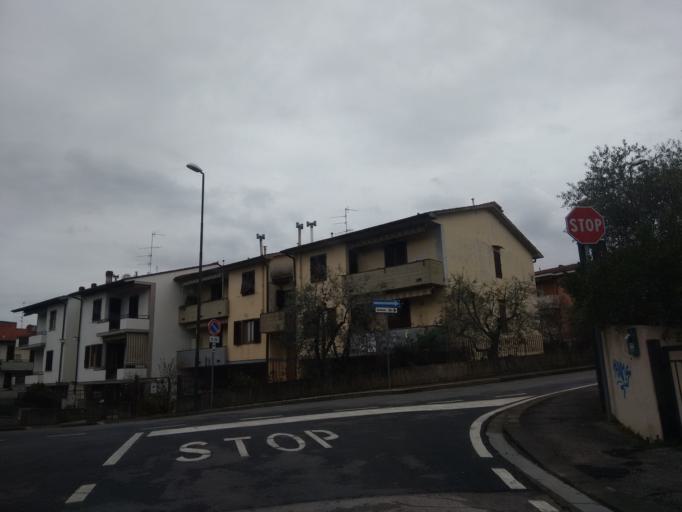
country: IT
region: Tuscany
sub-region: Province of Florence
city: Strada in Chianti
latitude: 43.6578
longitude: 11.2964
